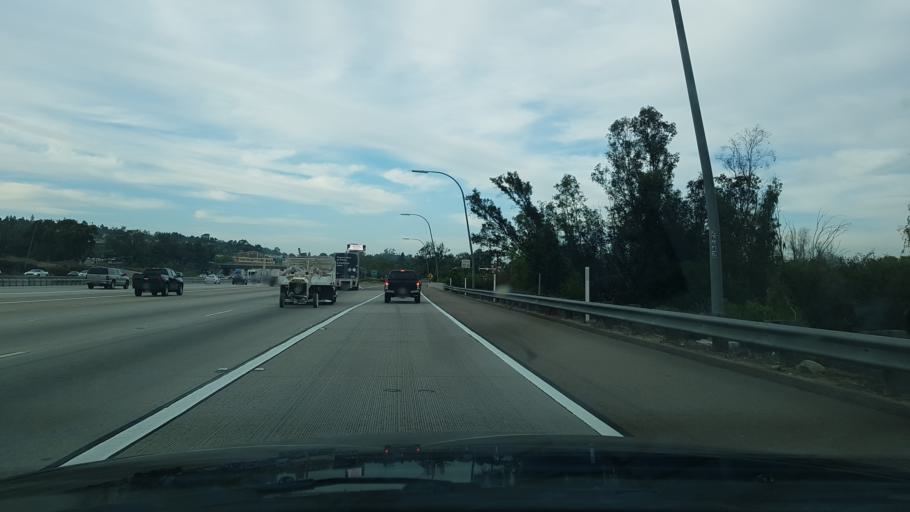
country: US
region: California
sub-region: San Diego County
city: Escondido
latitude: 33.0646
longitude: -117.0686
